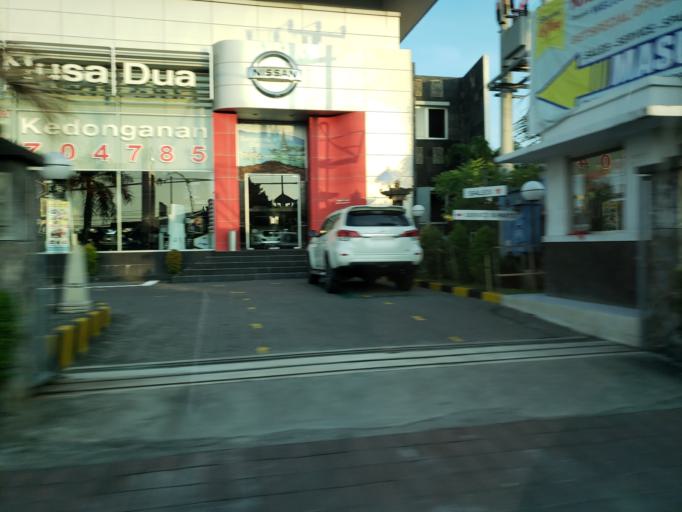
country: ID
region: Bali
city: Kelanabian
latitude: -8.7675
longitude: 115.1783
